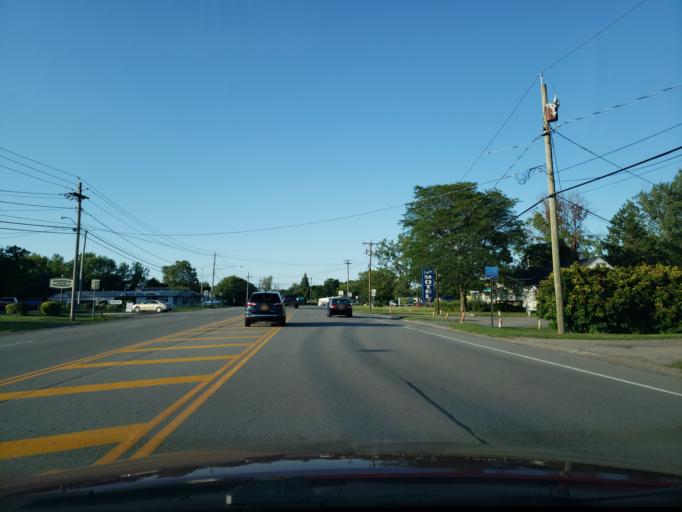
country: US
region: New York
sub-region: Monroe County
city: Webster
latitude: 43.1995
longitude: -77.4988
